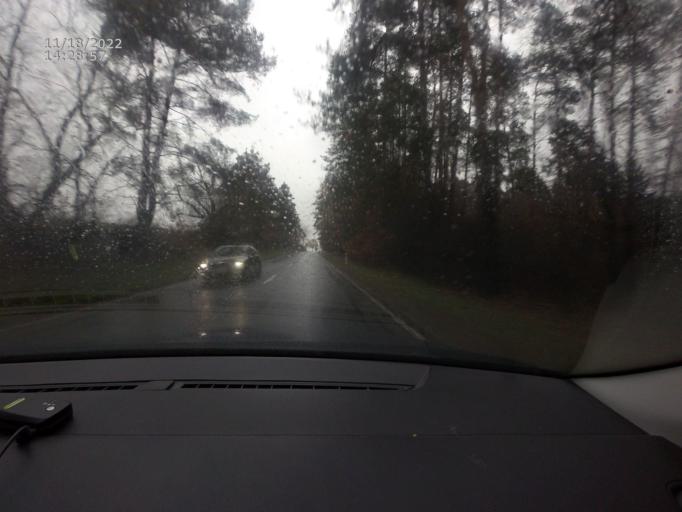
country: CZ
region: Jihocesky
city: Kovarov
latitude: 49.4301
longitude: 14.2289
